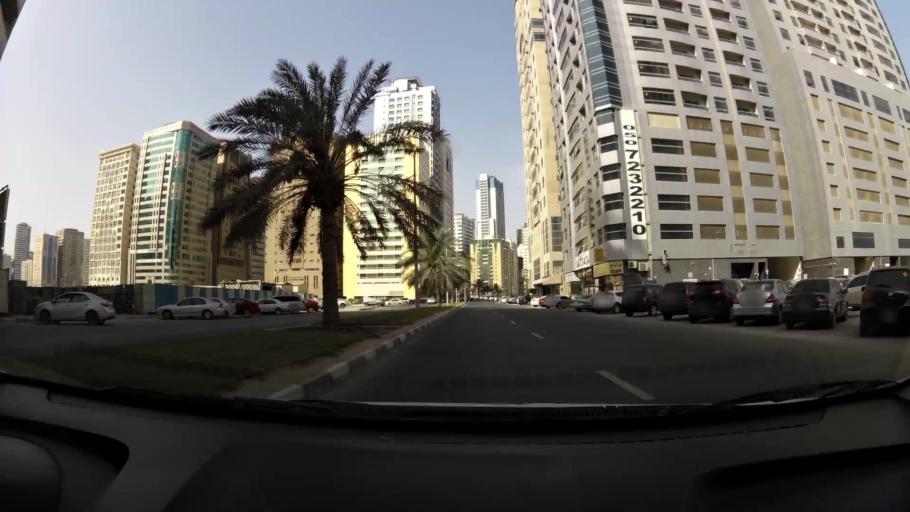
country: AE
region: Ash Shariqah
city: Sharjah
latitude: 25.3100
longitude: 55.3740
